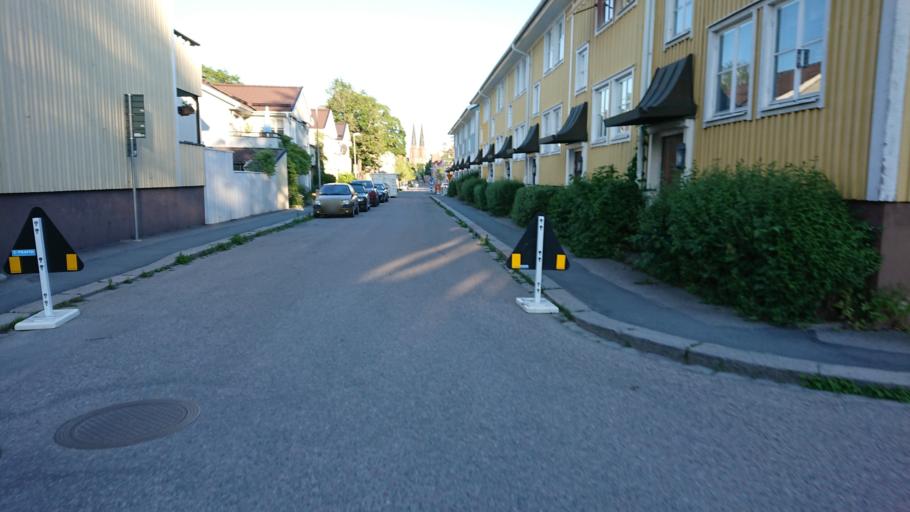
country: SE
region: Uppsala
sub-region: Uppsala Kommun
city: Uppsala
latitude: 59.8660
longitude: 17.6187
